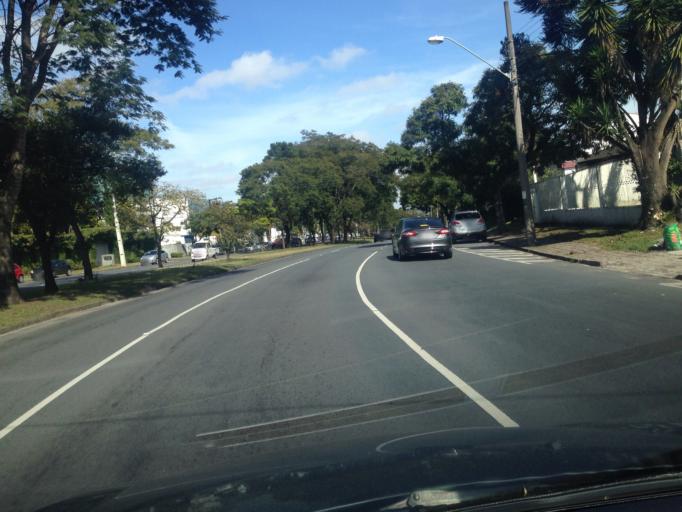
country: BR
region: Parana
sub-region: Curitiba
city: Curitiba
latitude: -25.4207
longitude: -49.2399
